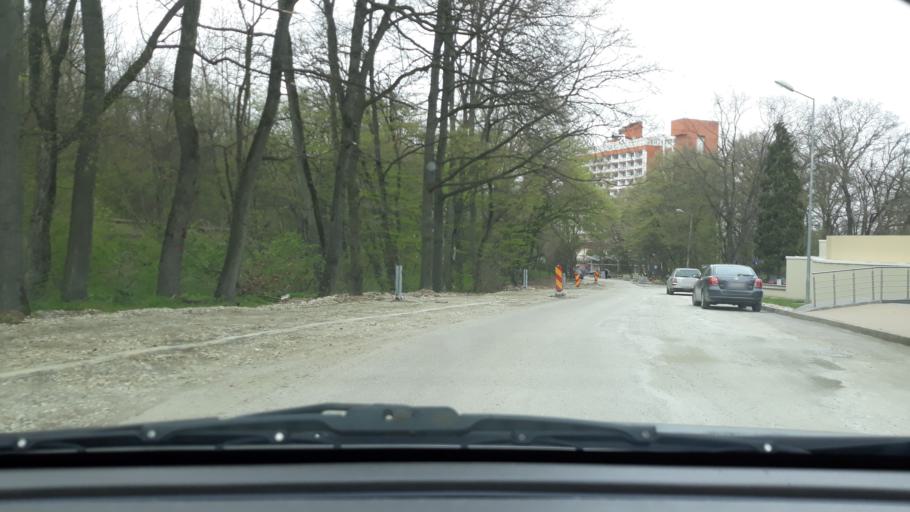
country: RO
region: Bihor
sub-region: Comuna Sanmartin
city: Sanmartin
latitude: 46.9898
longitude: 21.9754
